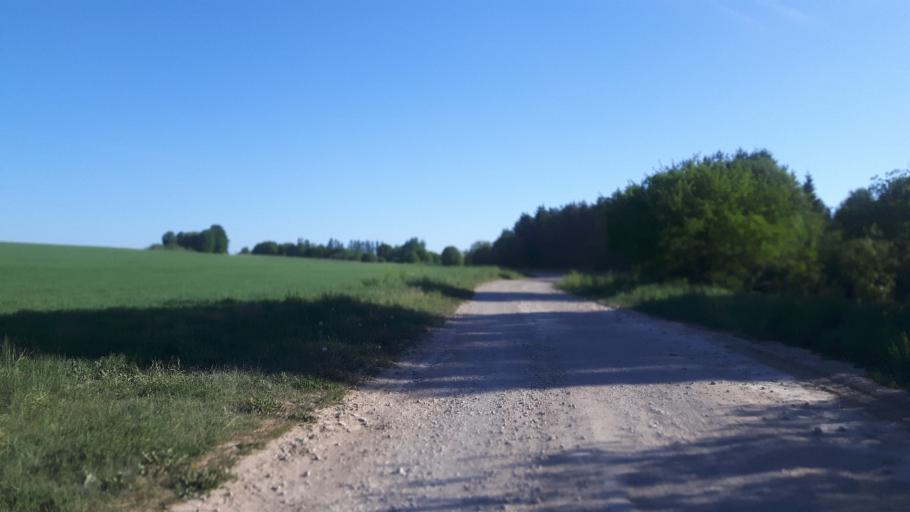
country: EE
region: Ida-Virumaa
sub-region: Puessi linn
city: Pussi
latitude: 59.4234
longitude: 27.0649
